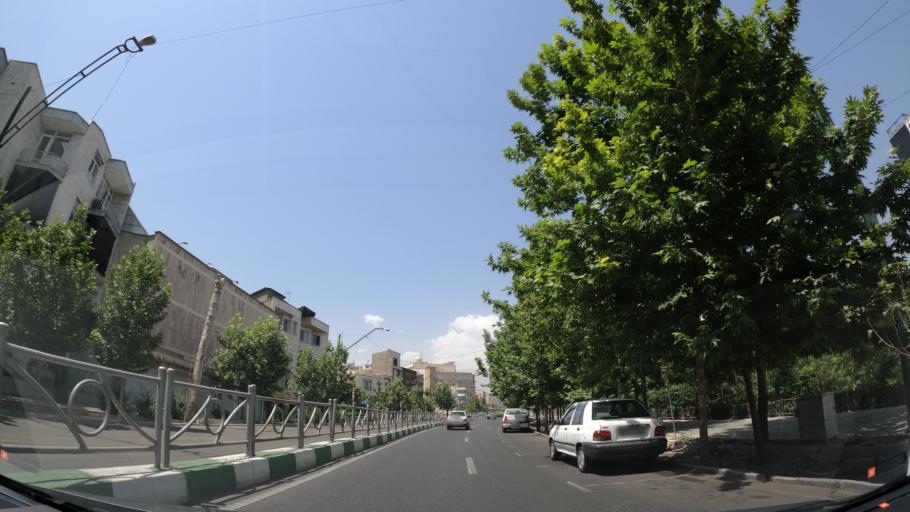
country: IR
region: Tehran
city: Tehran
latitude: 35.7378
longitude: 51.4091
